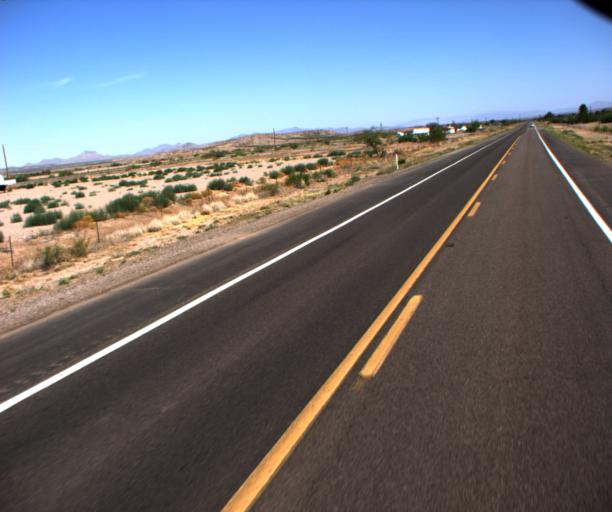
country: US
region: Arizona
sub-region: Greenlee County
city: Clifton
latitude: 32.6650
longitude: -109.0736
